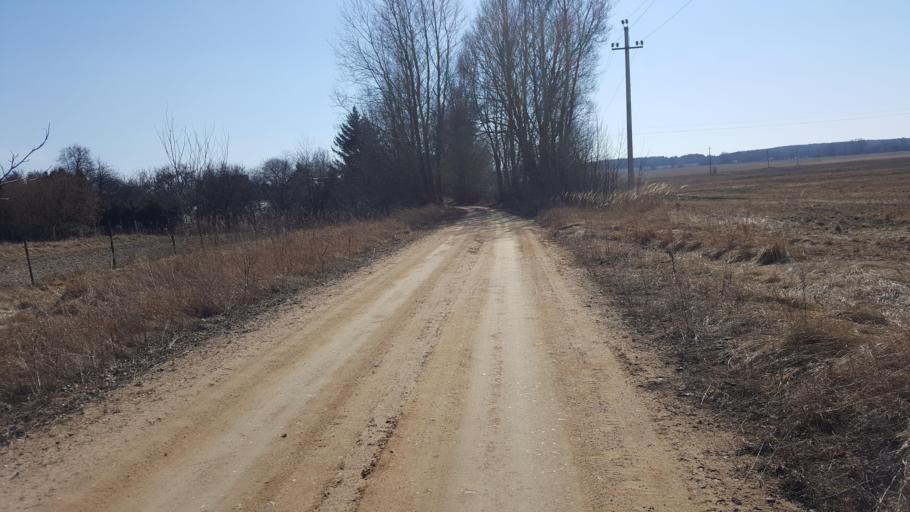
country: BY
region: Brest
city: Kamyanyets
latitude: 52.3637
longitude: 23.7618
